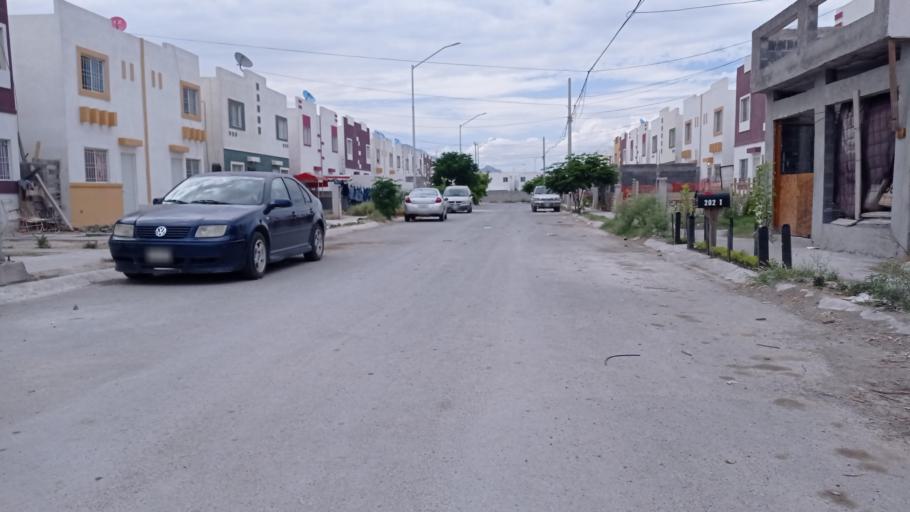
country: MX
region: Nuevo Leon
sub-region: Salinas Victoria
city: Simeprodeso (Colectivo Nuevo)
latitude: 25.8761
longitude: -100.3154
